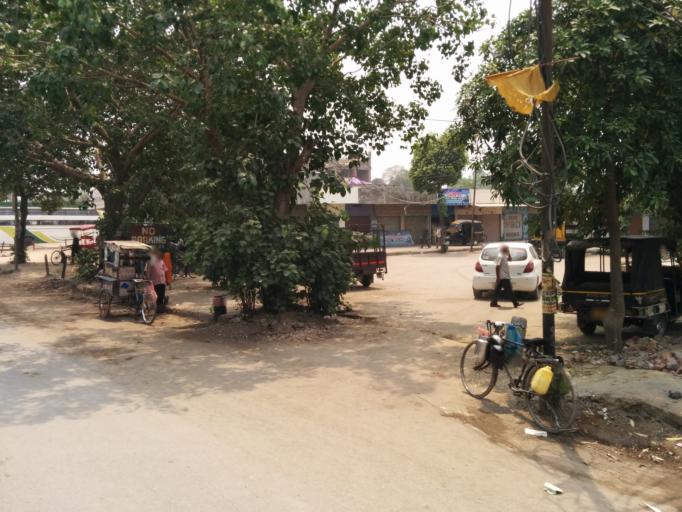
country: IN
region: Punjab
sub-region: Amritsar
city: Amritsar
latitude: 31.6279
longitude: 74.8873
